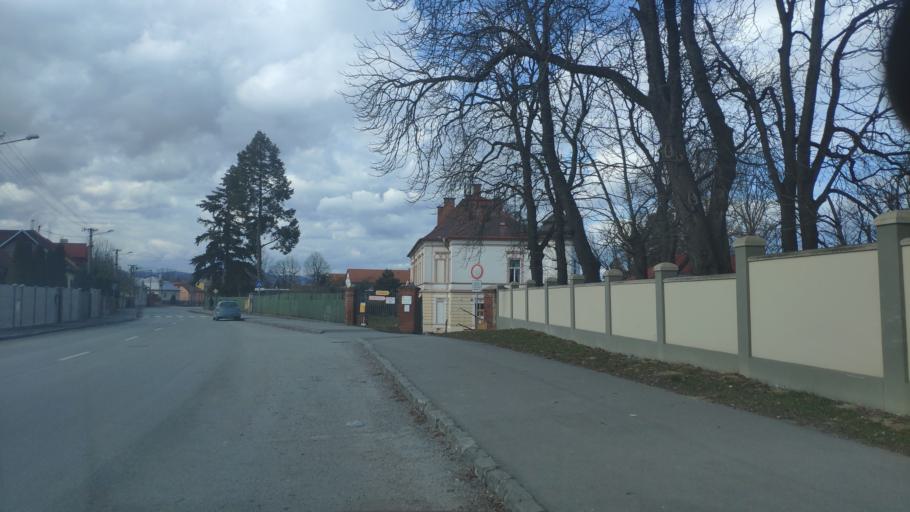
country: SK
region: Kosicky
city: Kosice
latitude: 48.6777
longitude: 21.2651
